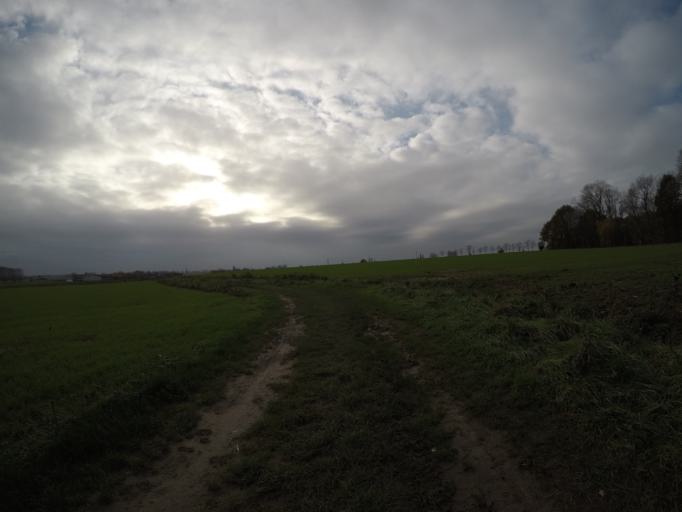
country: BE
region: Flanders
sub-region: Provincie West-Vlaanderen
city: Wervik
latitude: 50.8076
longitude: 3.0142
